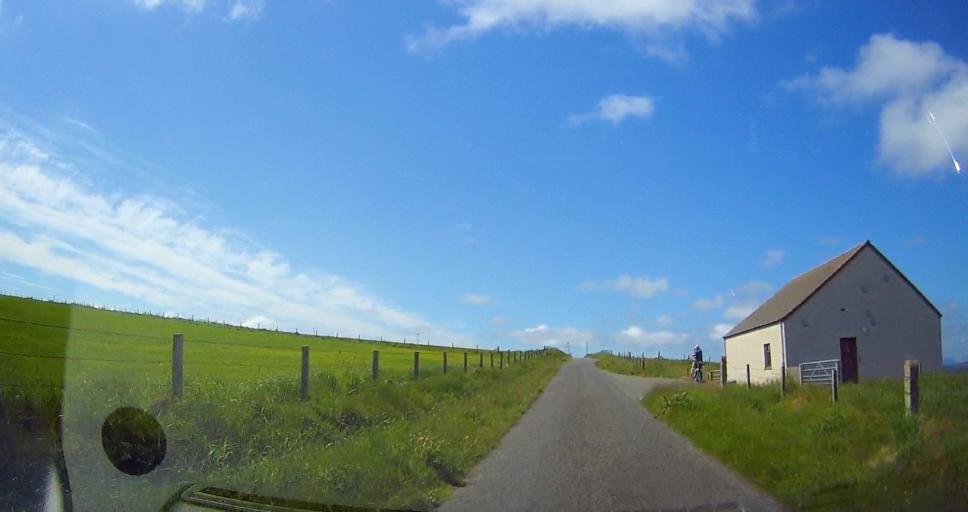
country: GB
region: Scotland
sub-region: Orkney Islands
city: Kirkwall
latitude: 58.8372
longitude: -2.9051
